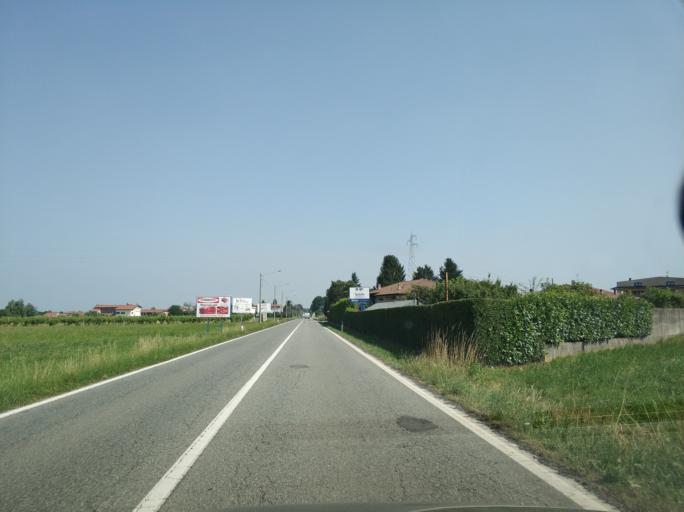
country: IT
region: Piedmont
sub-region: Provincia di Torino
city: Oglianico
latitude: 45.3483
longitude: 7.7037
